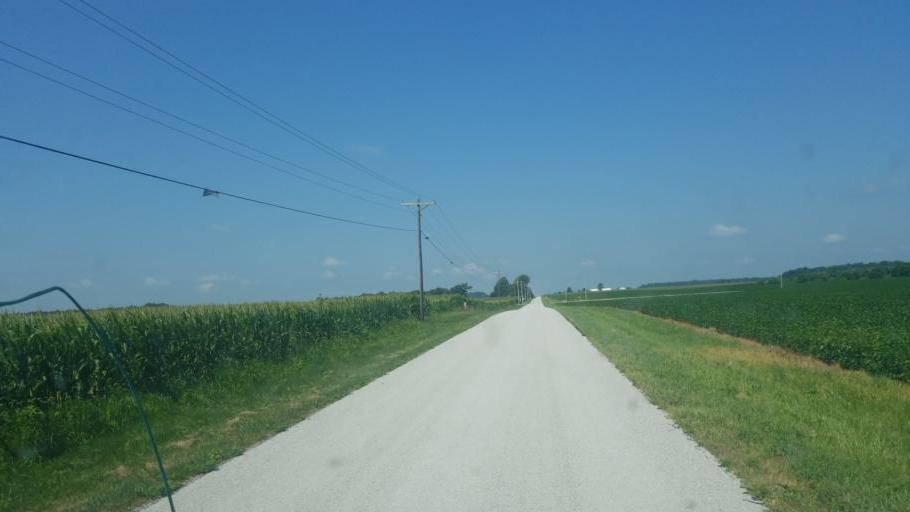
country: US
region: Ohio
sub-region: Hardin County
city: Kenton
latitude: 40.7032
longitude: -83.6695
